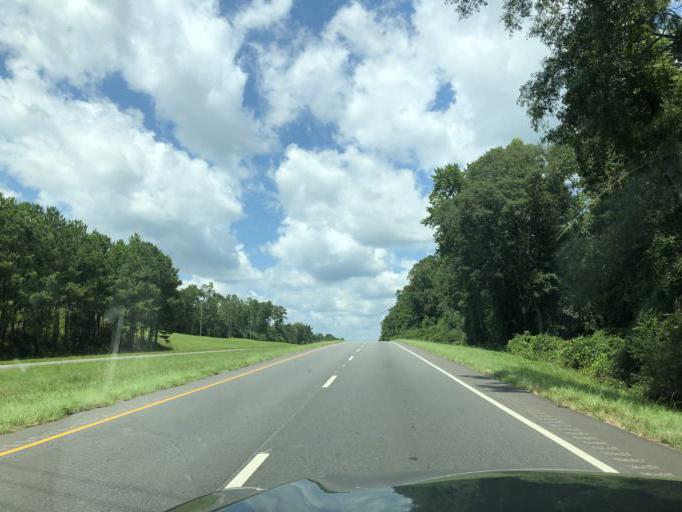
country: US
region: Alabama
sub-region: Barbour County
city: Eufaula
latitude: 31.9908
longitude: -85.1147
